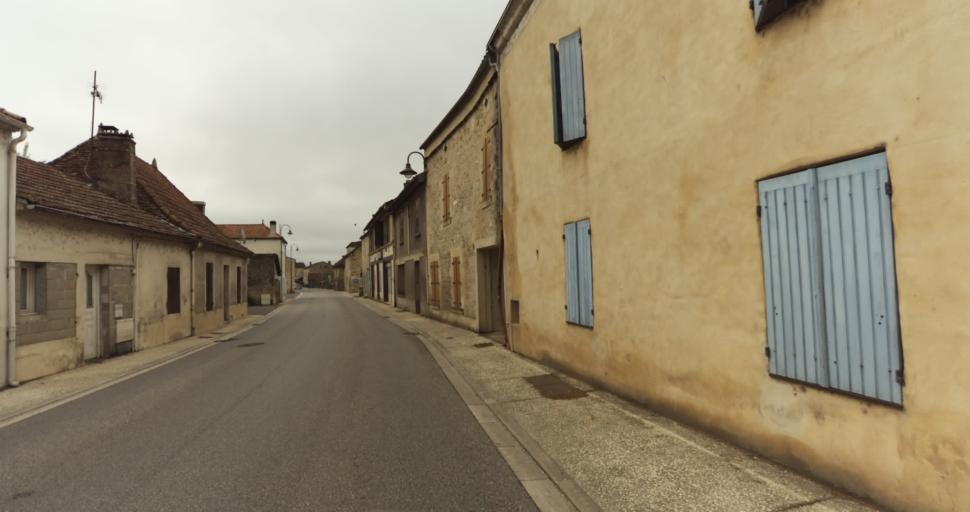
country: FR
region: Aquitaine
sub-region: Departement de la Dordogne
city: Mouleydier
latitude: 44.8425
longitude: 0.6505
